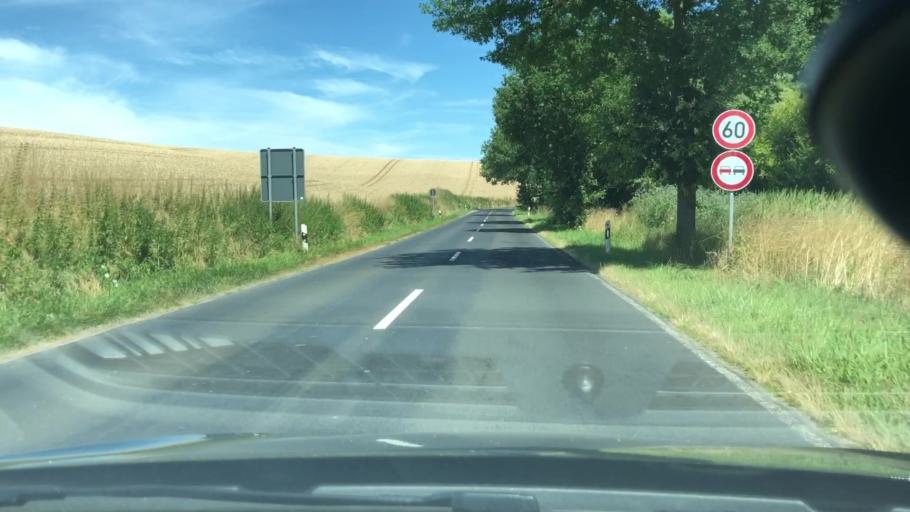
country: DE
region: Hesse
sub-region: Regierungsbezirk Darmstadt
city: Langenselbold
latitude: 50.2010
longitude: 9.0236
